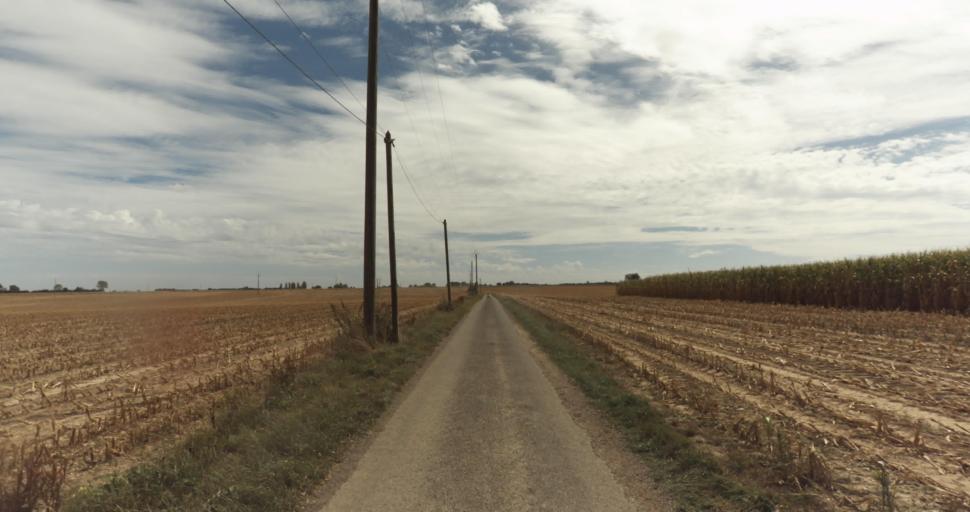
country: FR
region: Lower Normandy
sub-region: Departement du Calvados
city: Orbec
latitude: 48.9554
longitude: 0.3955
